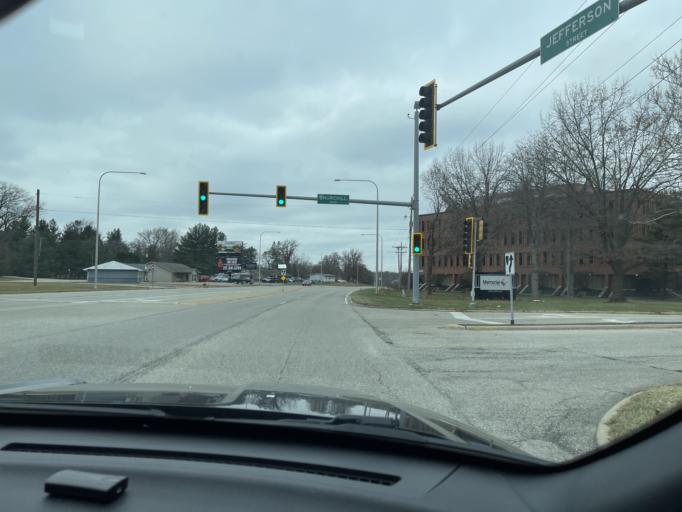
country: US
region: Illinois
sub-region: Sangamon County
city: Leland Grove
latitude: 39.8121
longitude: -89.6945
